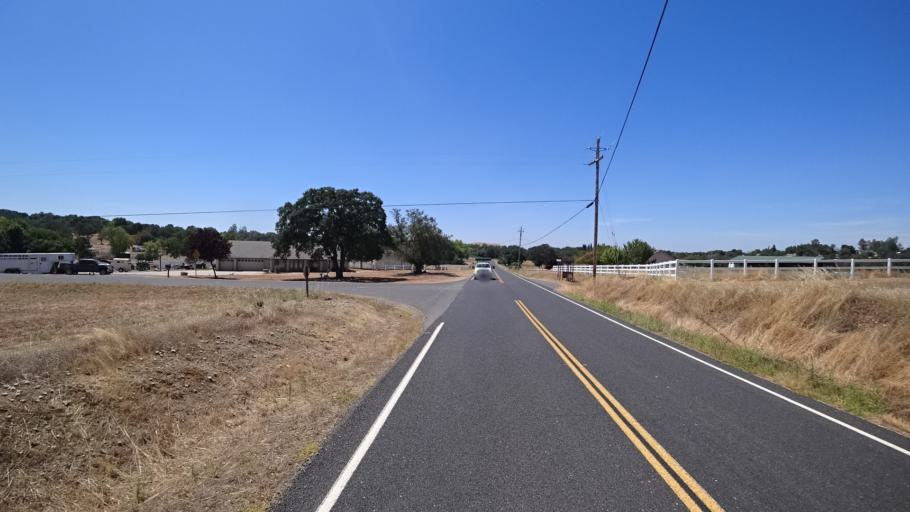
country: US
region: California
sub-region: Calaveras County
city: Rancho Calaveras
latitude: 38.1542
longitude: -120.9439
